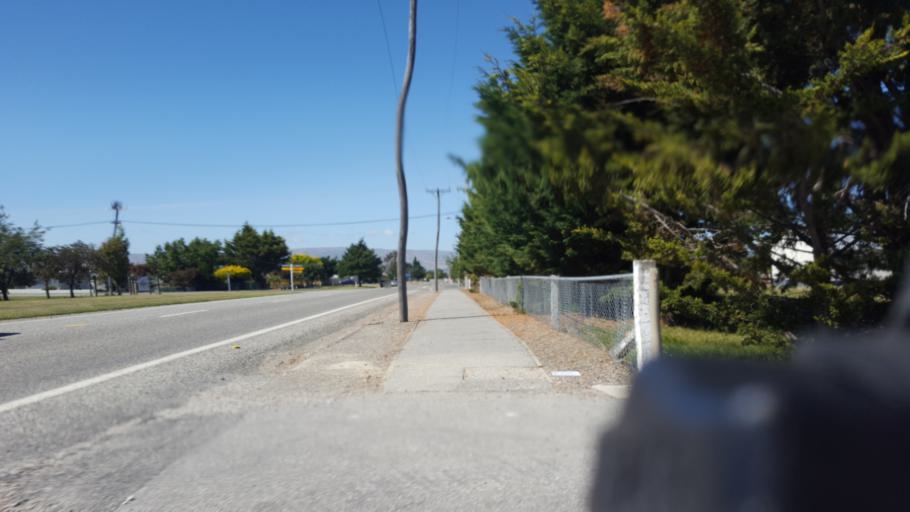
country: NZ
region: Otago
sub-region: Dunedin City
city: Dunedin
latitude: -45.1249
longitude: 170.1004
